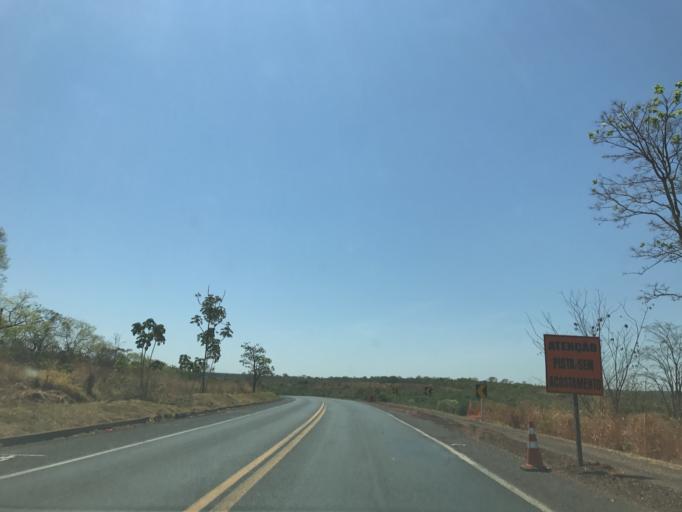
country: BR
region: Minas Gerais
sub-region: Prata
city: Prata
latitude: -19.4213
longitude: -48.8894
